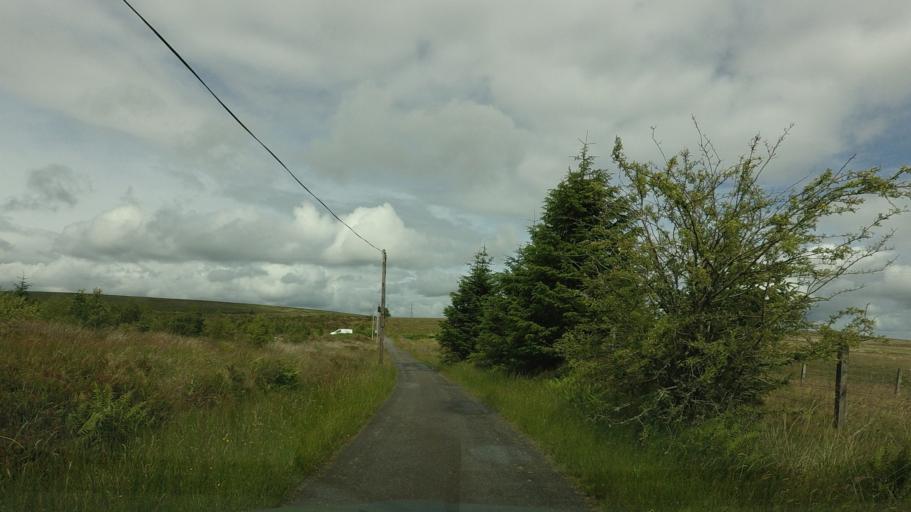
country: GB
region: Scotland
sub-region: Stirling
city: Killearn
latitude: 56.0917
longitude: -4.4324
